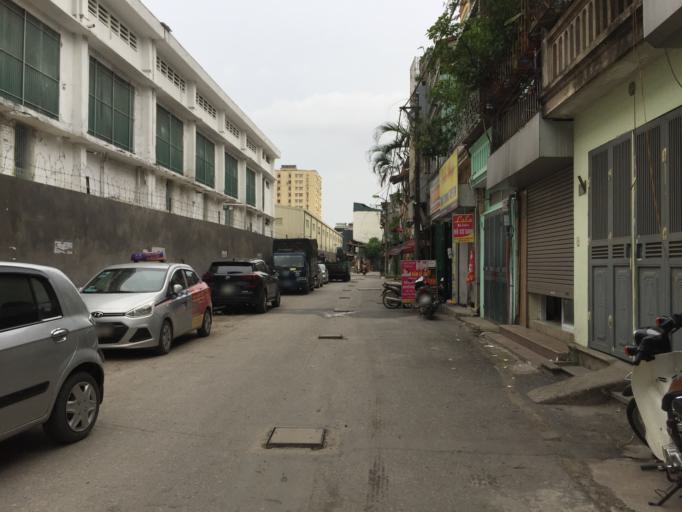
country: VN
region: Ha Noi
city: Thanh Xuan
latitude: 20.9890
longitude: 105.8085
